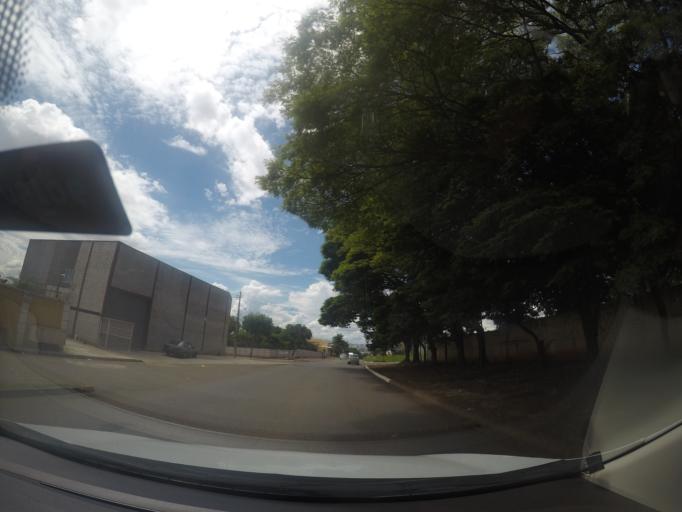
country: BR
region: Goias
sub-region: Goiania
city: Goiania
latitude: -16.6612
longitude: -49.3360
